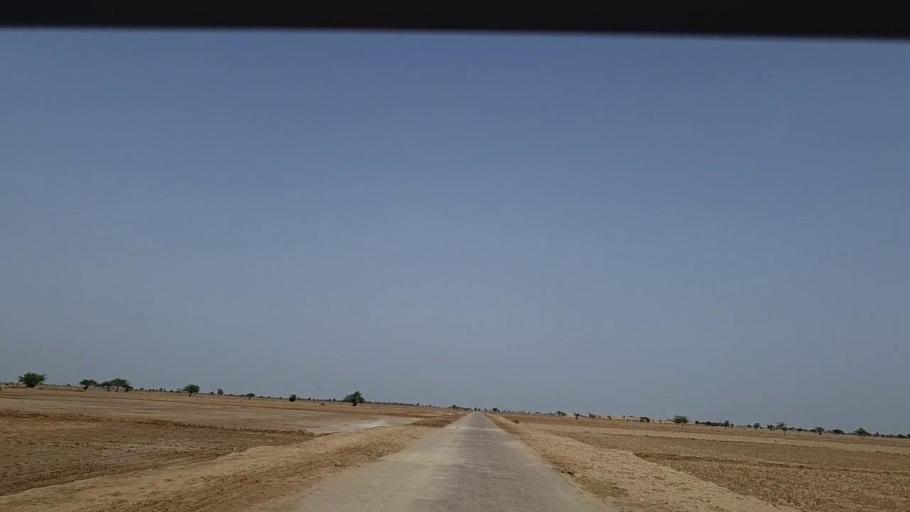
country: PK
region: Sindh
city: Johi
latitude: 26.7706
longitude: 67.6379
